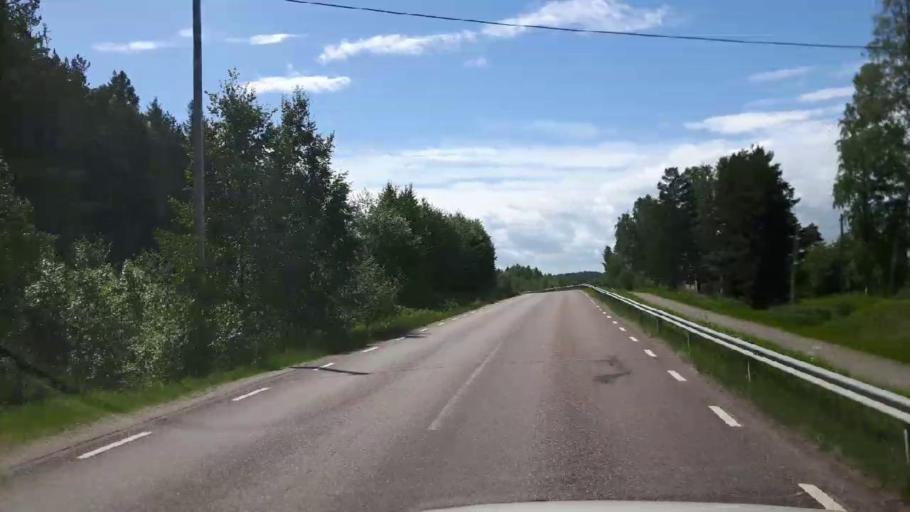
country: SE
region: Dalarna
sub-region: Faluns Kommun
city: Falun
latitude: 60.6125
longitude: 15.7751
